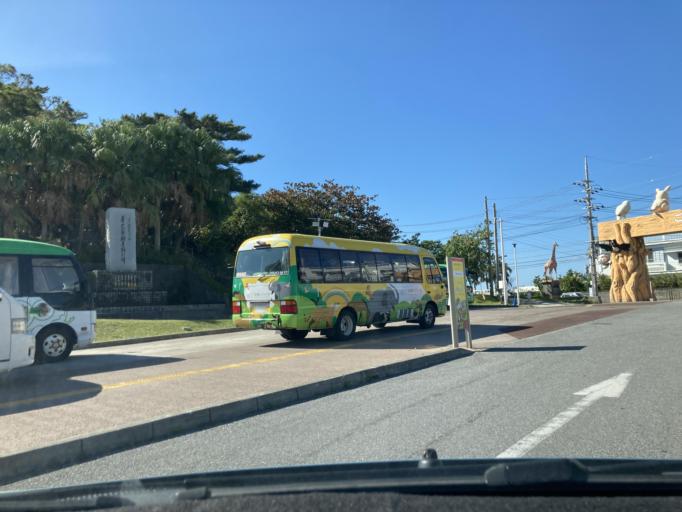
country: JP
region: Okinawa
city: Okinawa
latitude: 26.3277
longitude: 127.8031
